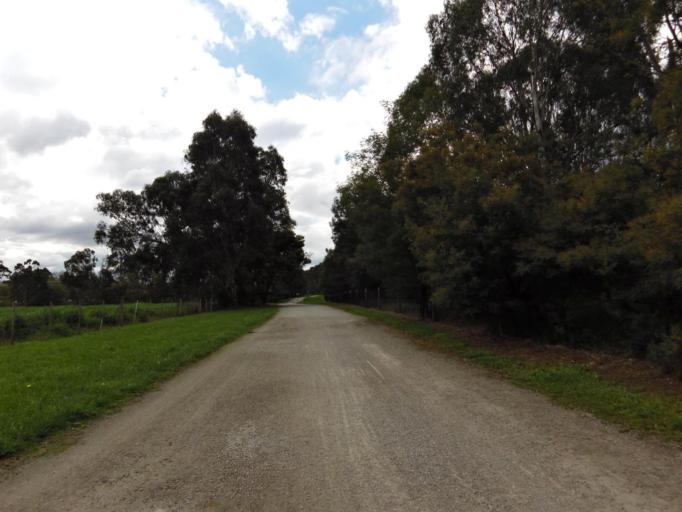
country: AU
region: Victoria
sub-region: Manningham
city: Bulleen
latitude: -37.7646
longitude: 145.0730
